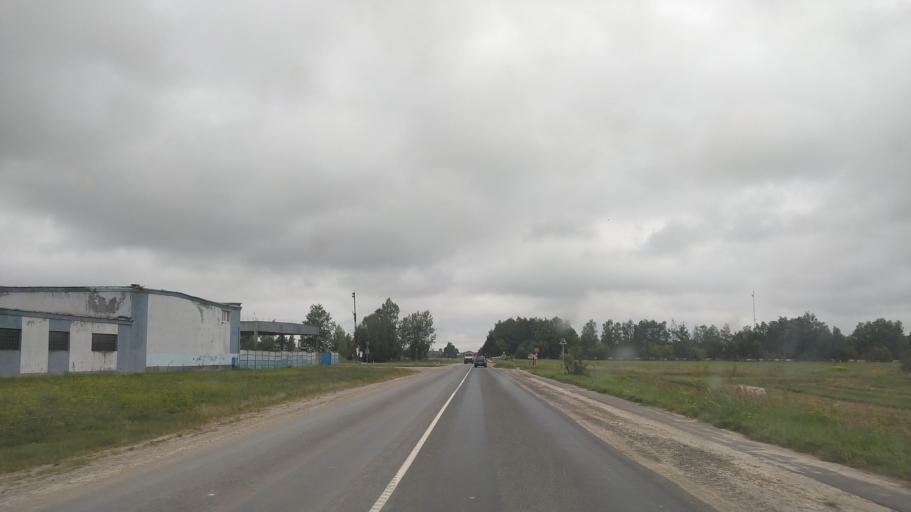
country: BY
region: Brest
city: Byaroza
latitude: 52.5521
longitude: 24.9338
